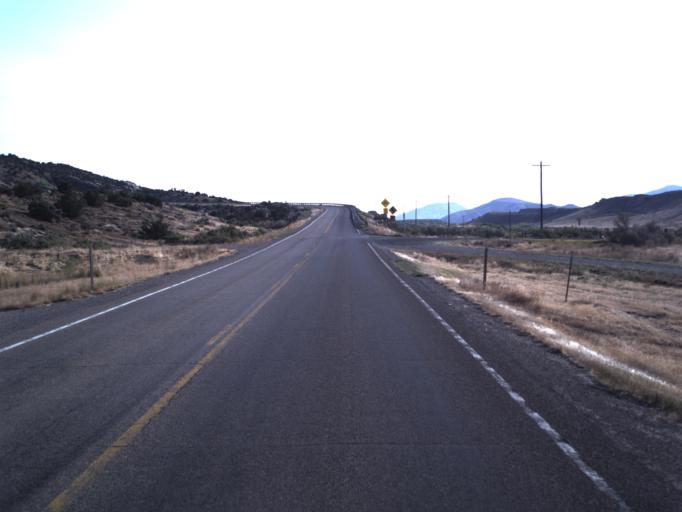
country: US
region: Utah
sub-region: Uintah County
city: Vernal
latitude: 40.5076
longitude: -109.5264
